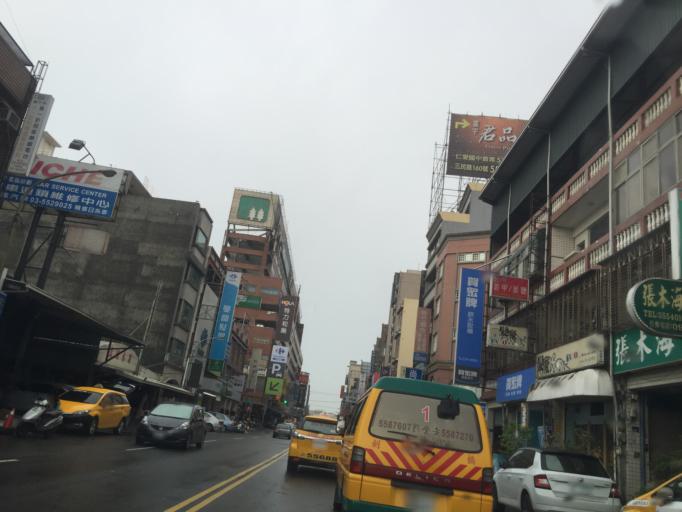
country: TW
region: Taiwan
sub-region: Hsinchu
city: Zhubei
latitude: 24.8248
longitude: 121.0085
